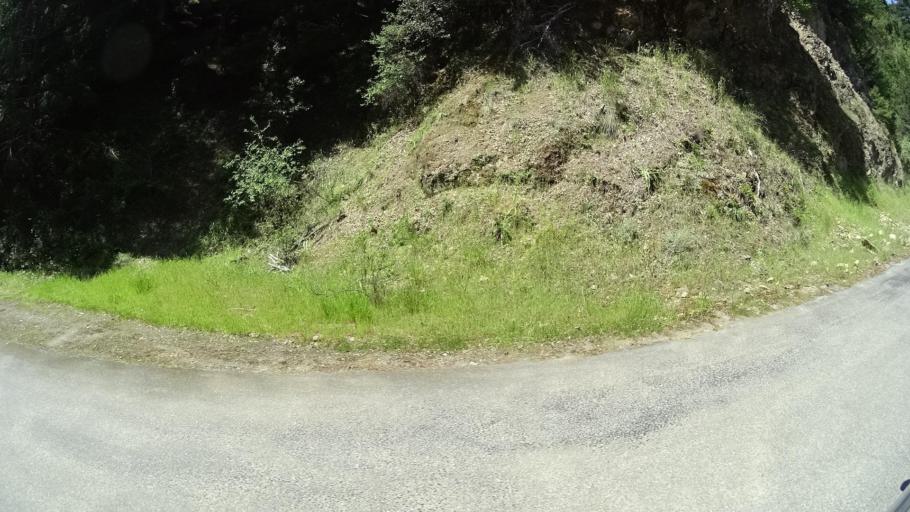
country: US
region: California
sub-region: Humboldt County
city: Redway
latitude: 40.1941
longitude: -123.5266
